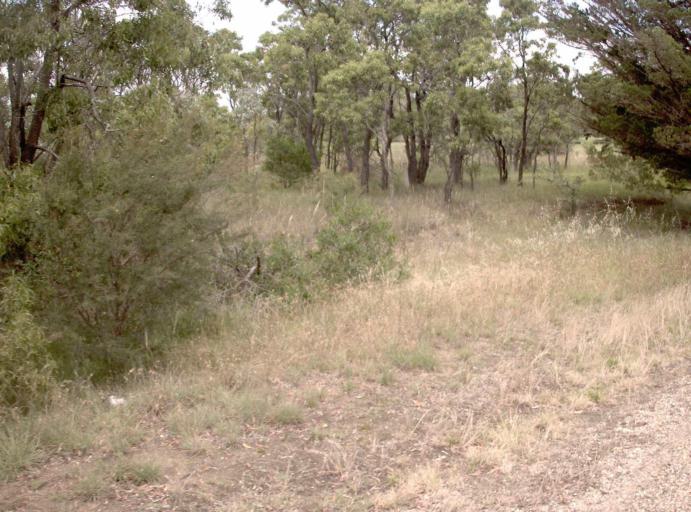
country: AU
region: Victoria
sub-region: Wellington
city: Sale
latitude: -37.9747
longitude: 147.0105
